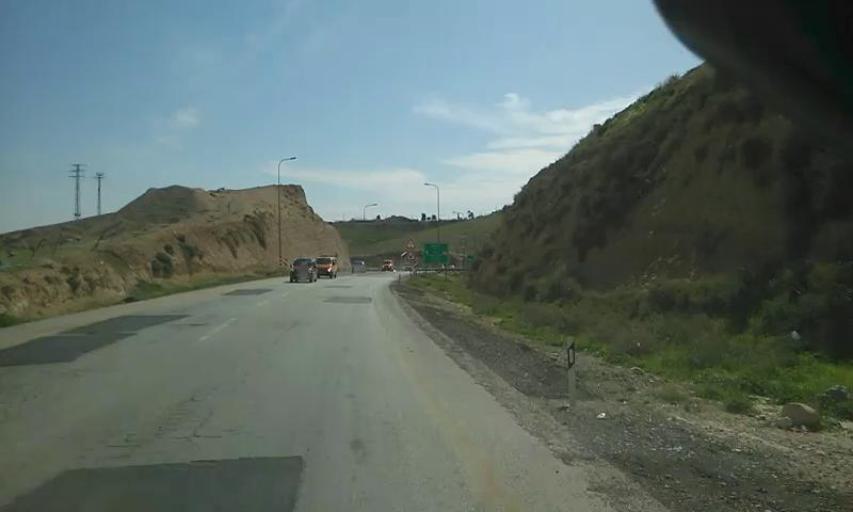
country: PS
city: Az Za`ayyim
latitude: 31.8068
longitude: 35.3243
